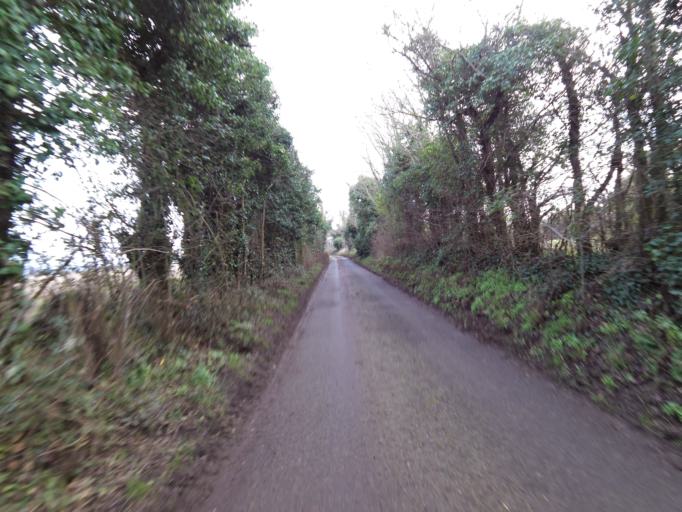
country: GB
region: England
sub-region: Suffolk
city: Woodbridge
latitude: 52.0591
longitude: 1.3167
